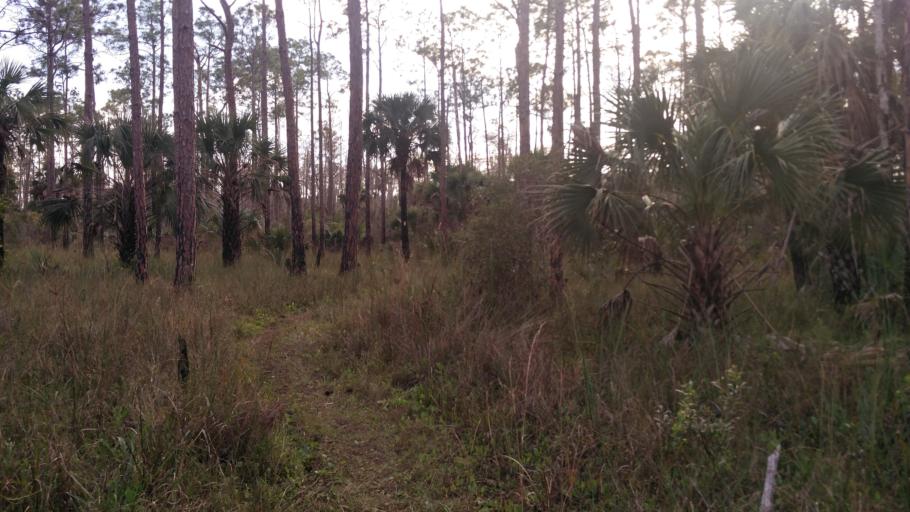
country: US
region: Florida
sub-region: Collier County
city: Lely Resort
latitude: 26.0020
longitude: -81.5826
